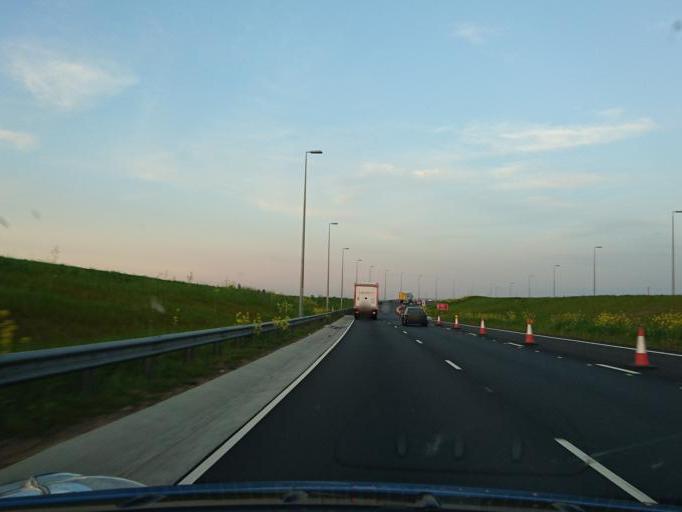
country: GB
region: England
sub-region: Leicestershire
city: Lutterworth
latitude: 52.4054
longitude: -1.1857
